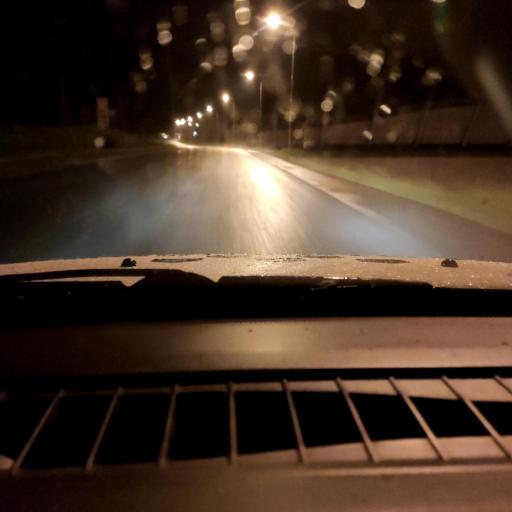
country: RU
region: Udmurtiya
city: Khokhryaki
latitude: 57.1715
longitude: 53.1602
